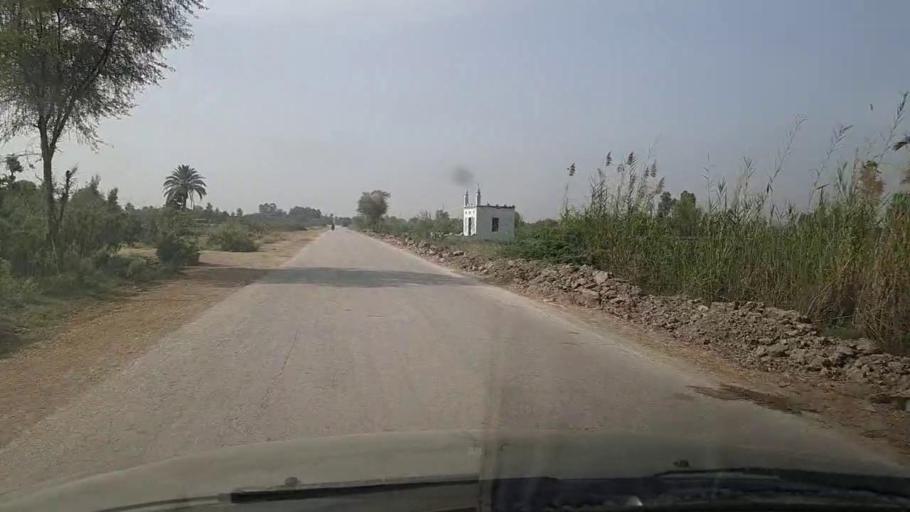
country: PK
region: Sindh
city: Gambat
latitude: 27.4460
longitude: 68.4861
